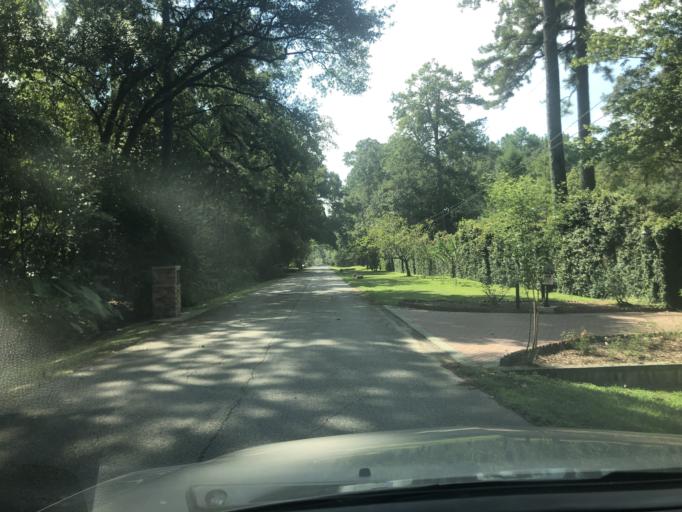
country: US
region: Texas
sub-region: Harris County
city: Bunker Hill Village
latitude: 29.7497
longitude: -95.5460
